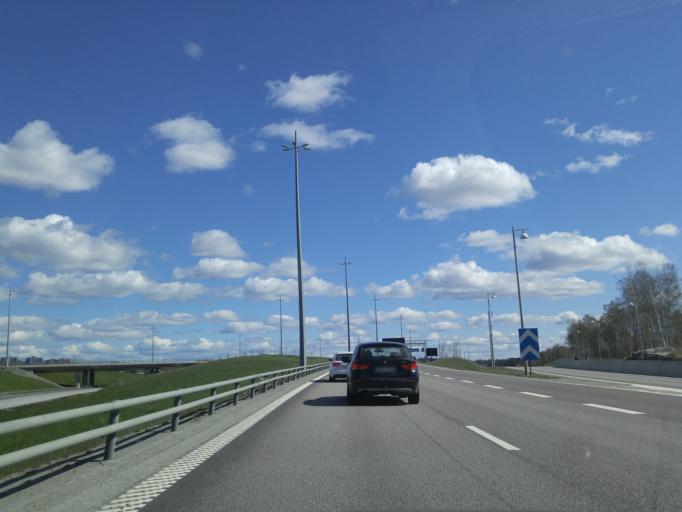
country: SE
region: Vaestra Goetaland
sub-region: Goteborg
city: Majorna
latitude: 57.7045
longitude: 11.8696
